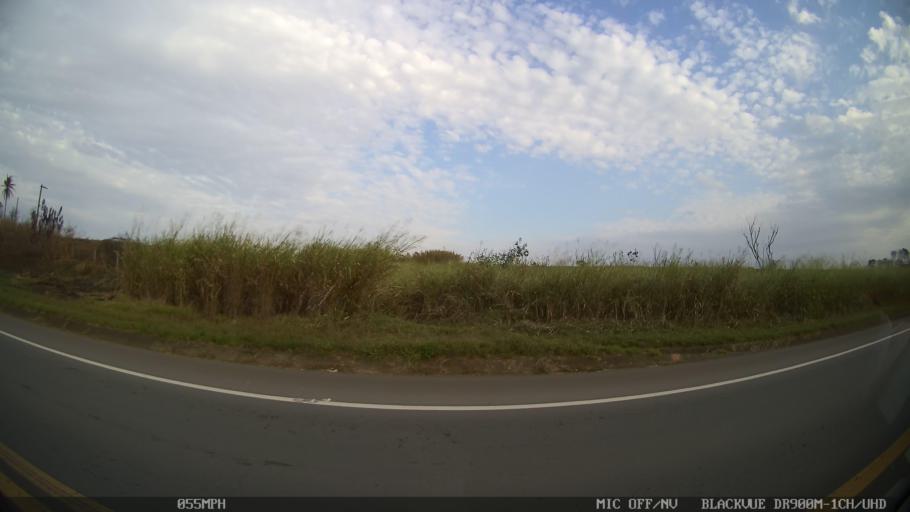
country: BR
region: Sao Paulo
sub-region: Cosmopolis
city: Cosmopolis
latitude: -22.6313
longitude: -47.2951
